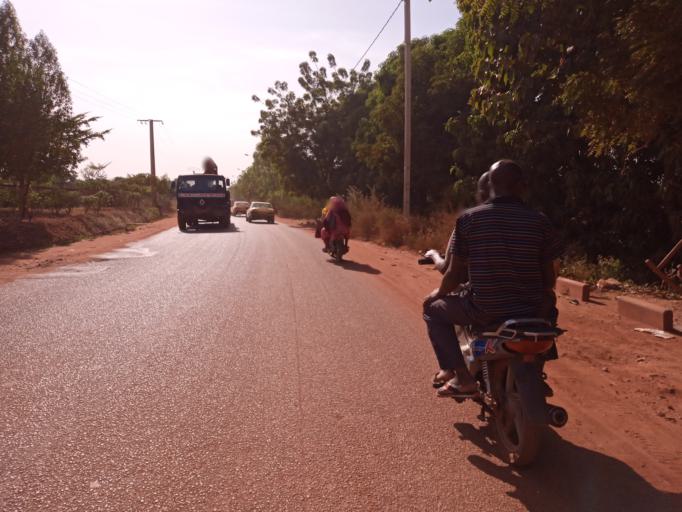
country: ML
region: Bamako
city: Bamako
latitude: 12.6341
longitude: -7.9372
